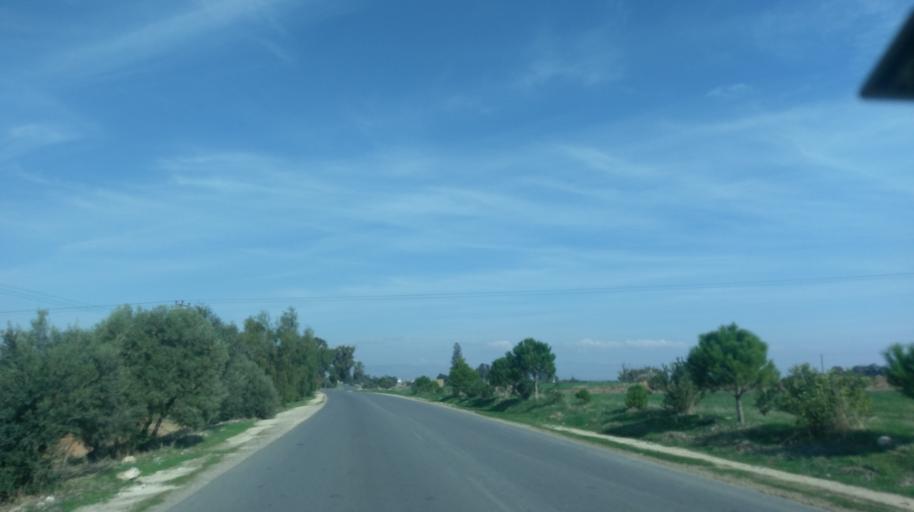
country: CY
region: Larnaka
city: Troulloi
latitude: 35.1494
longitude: 33.6371
